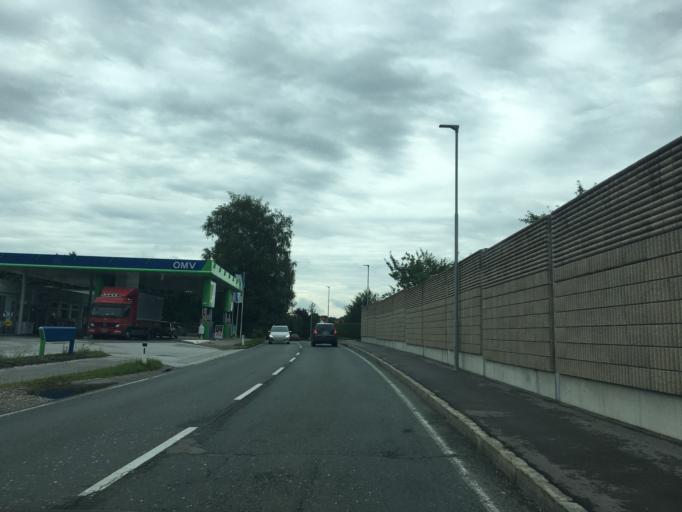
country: AT
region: Salzburg
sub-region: Politischer Bezirk Salzburg-Umgebung
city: Lamprechtshausen
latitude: 47.9860
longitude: 12.9546
